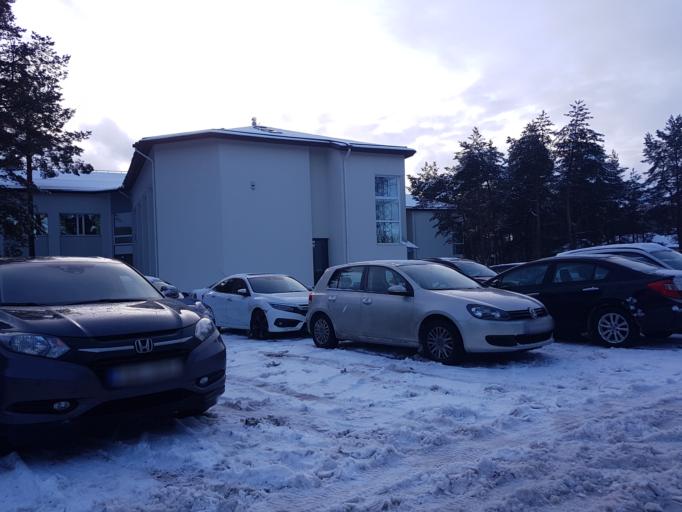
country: EE
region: Harju
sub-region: Saue vald
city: Laagri
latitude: 59.3586
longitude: 24.6321
